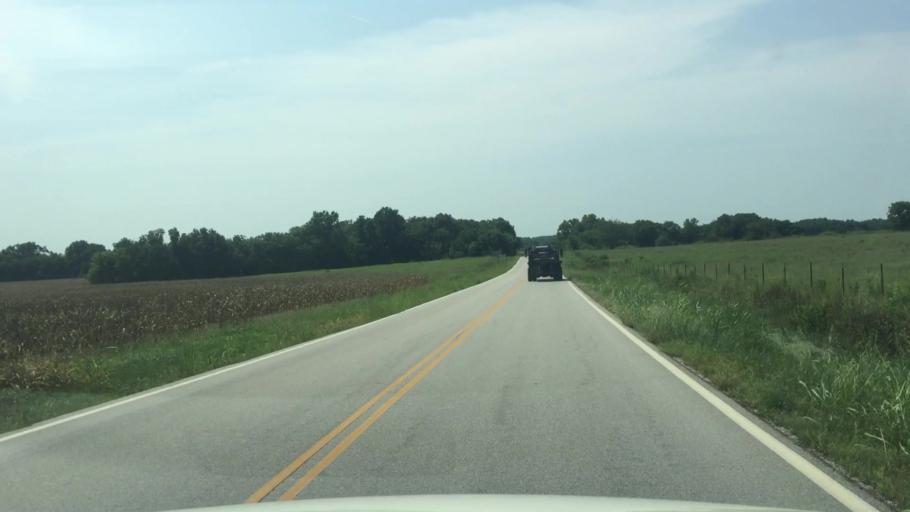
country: US
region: Kansas
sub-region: Montgomery County
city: Cherryvale
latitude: 37.2062
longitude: -95.5576
